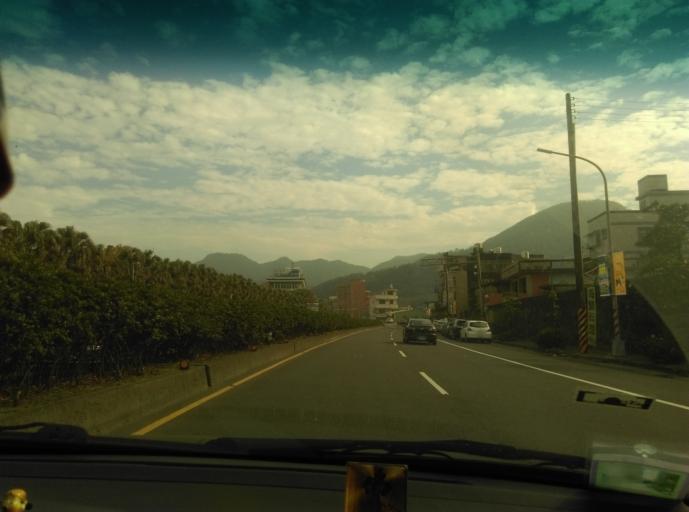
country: TW
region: Taiwan
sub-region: Keelung
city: Keelung
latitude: 25.1816
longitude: 121.6890
